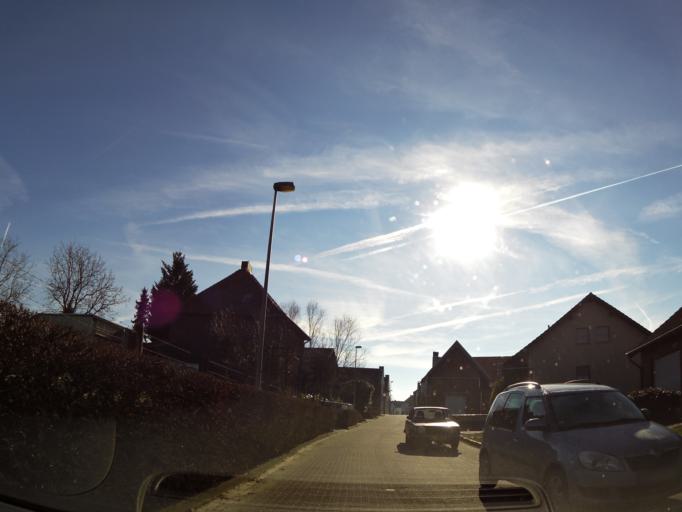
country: NL
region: Limburg
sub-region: Gemeente Sittard-Geleen
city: Sittard
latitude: 51.0278
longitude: 5.8764
